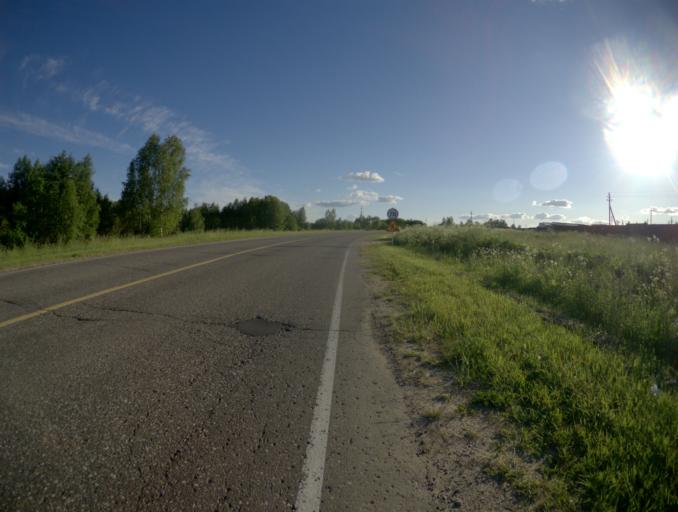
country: RU
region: Ivanovo
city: Lezhnevo
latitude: 56.8247
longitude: 40.8757
